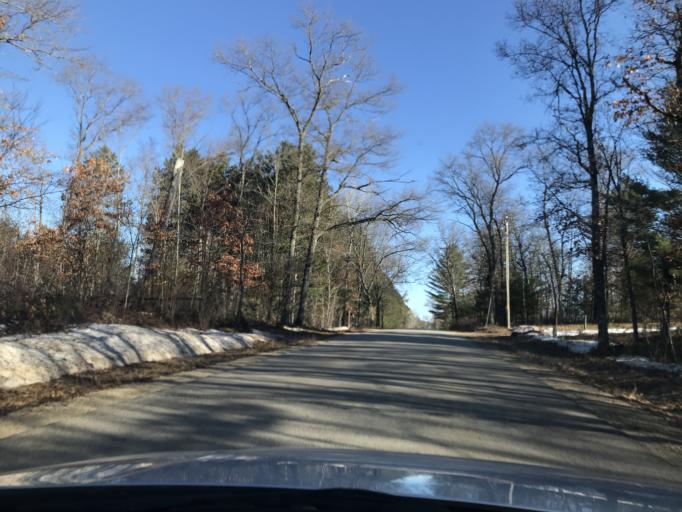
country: US
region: Wisconsin
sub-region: Marinette County
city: Niagara
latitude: 45.3920
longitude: -88.0790
